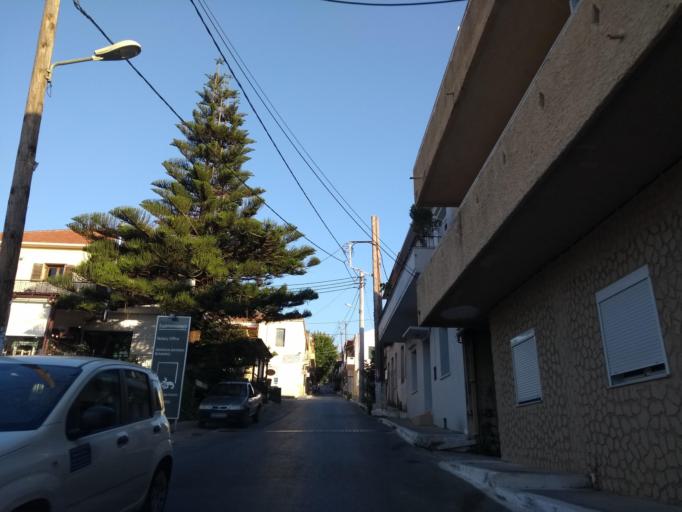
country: GR
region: Crete
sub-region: Nomos Chanias
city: Kalivai
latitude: 35.4082
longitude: 24.1982
